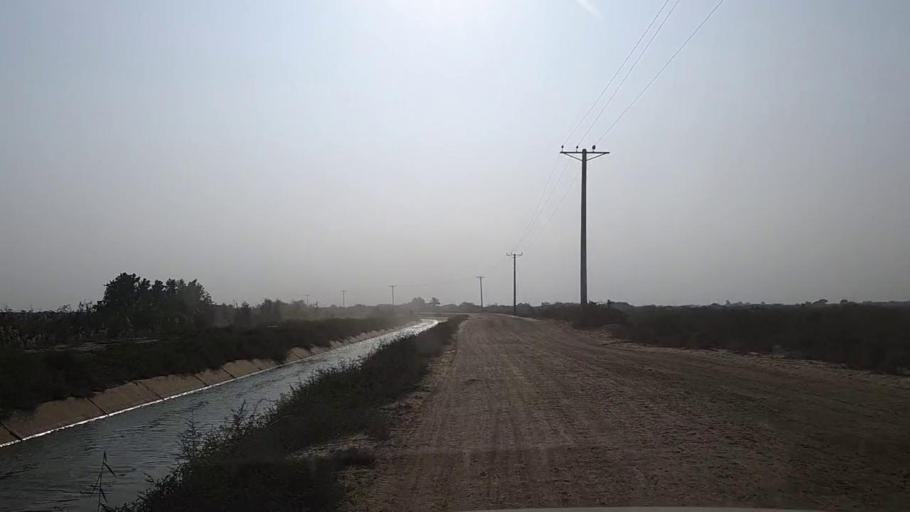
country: PK
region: Sindh
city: Keti Bandar
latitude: 24.1936
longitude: 67.6126
